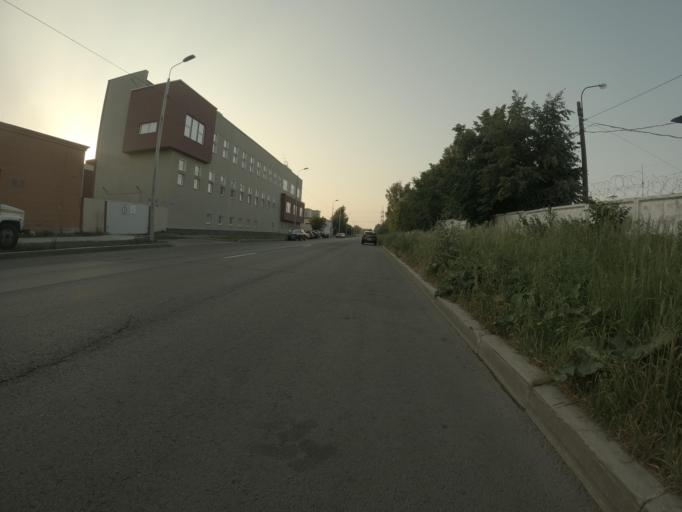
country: RU
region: St.-Petersburg
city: Krasnogvargeisky
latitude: 59.9708
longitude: 30.4409
